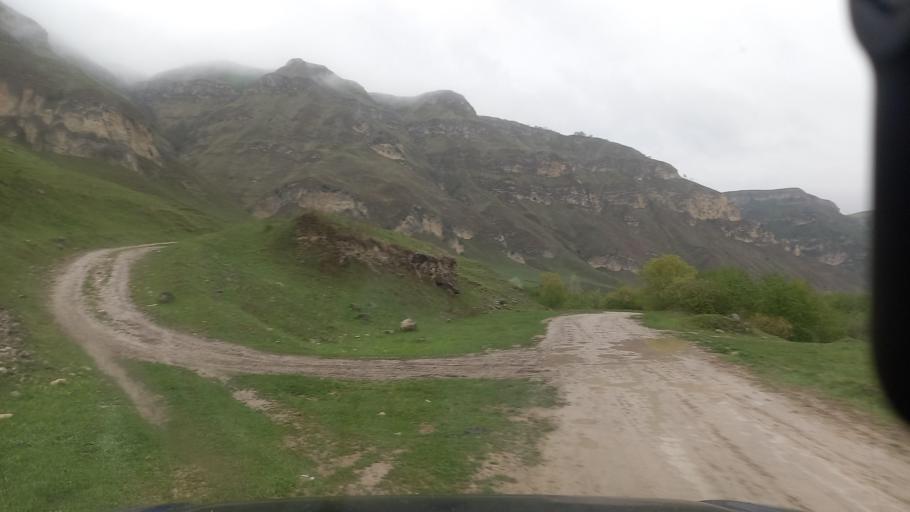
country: RU
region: Kabardino-Balkariya
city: Bylym
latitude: 43.5932
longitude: 43.0320
